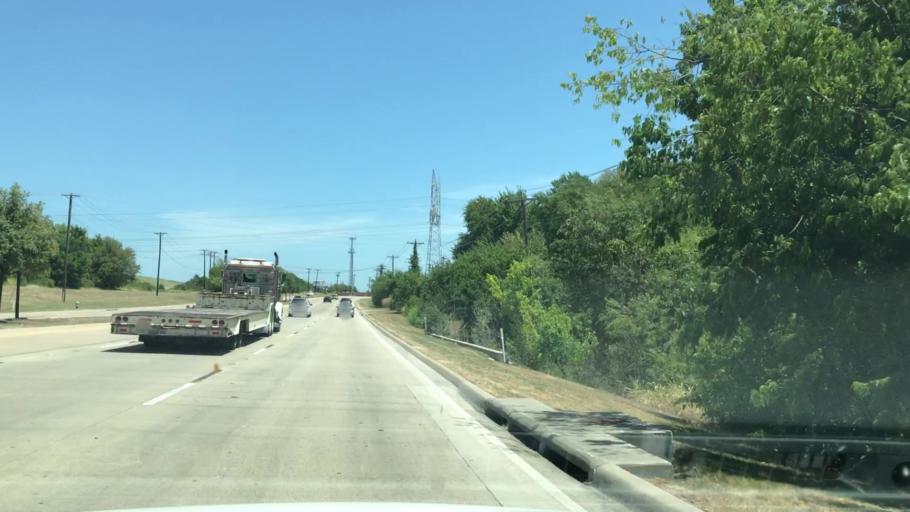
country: US
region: Texas
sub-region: Collin County
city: Wylie
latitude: 33.0202
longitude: -96.5266
